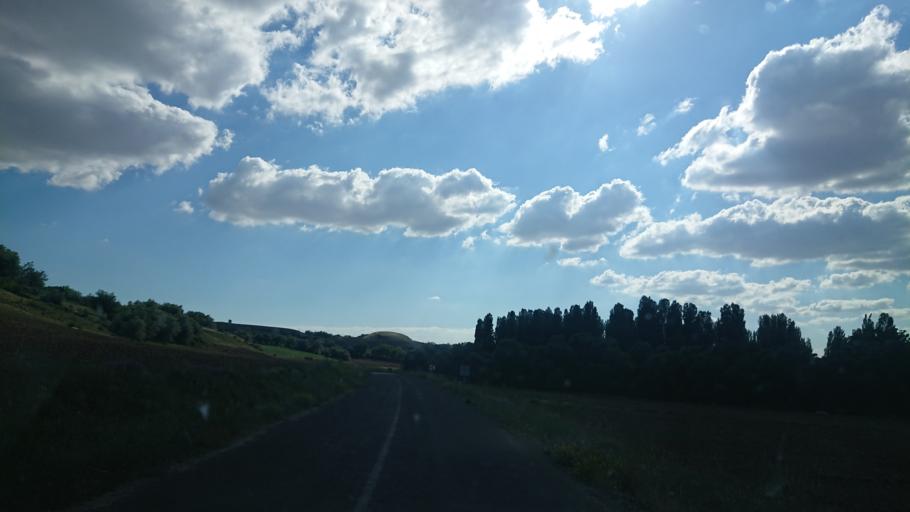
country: TR
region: Aksaray
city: Agacoren
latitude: 38.7577
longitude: 33.8988
